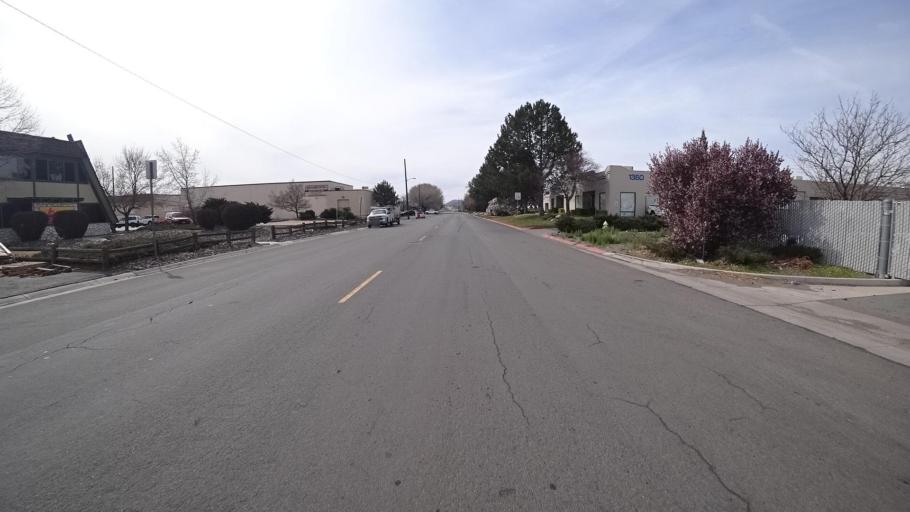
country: US
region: Nevada
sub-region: Washoe County
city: Sparks
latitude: 39.5270
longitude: -119.7584
